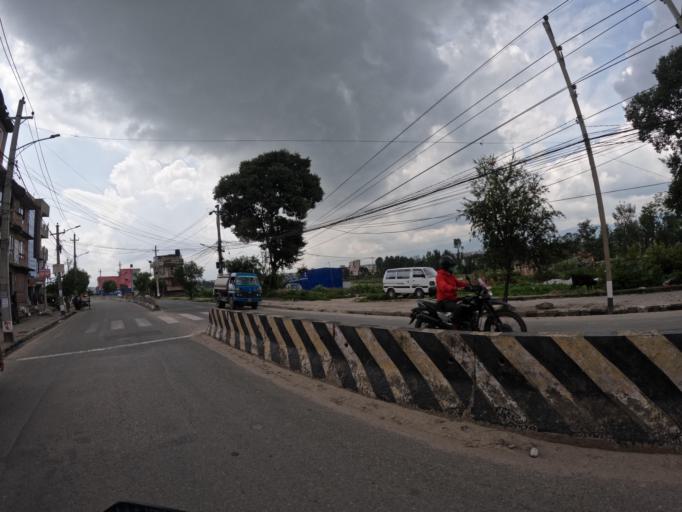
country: NP
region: Central Region
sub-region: Bagmati Zone
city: Bhaktapur
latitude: 27.6761
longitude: 85.4174
